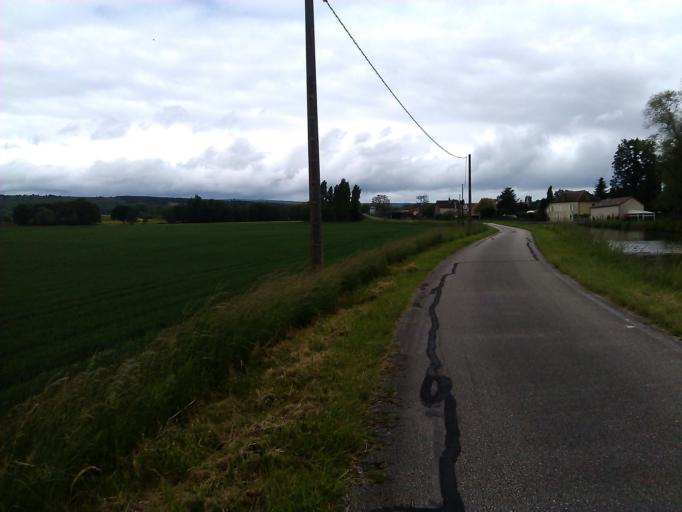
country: FR
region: Bourgogne
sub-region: Departement de Saone-et-Loire
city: Fontaines
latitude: 46.8763
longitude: 4.7734
